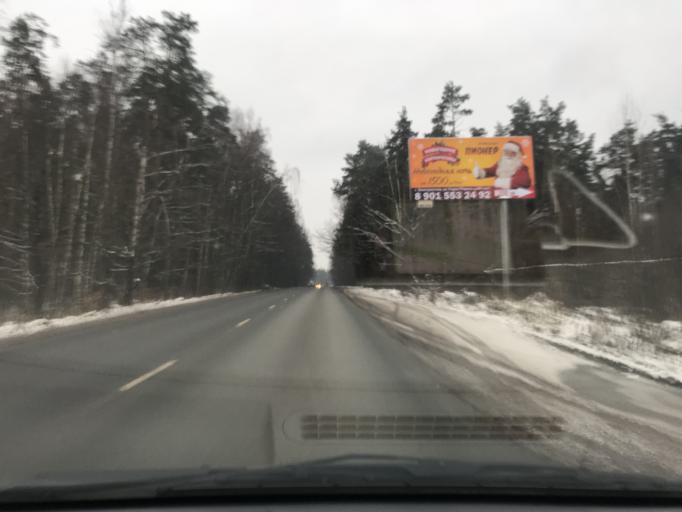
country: RU
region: Moskovskaya
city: Elektrostal'
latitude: 55.8262
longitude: 38.4522
